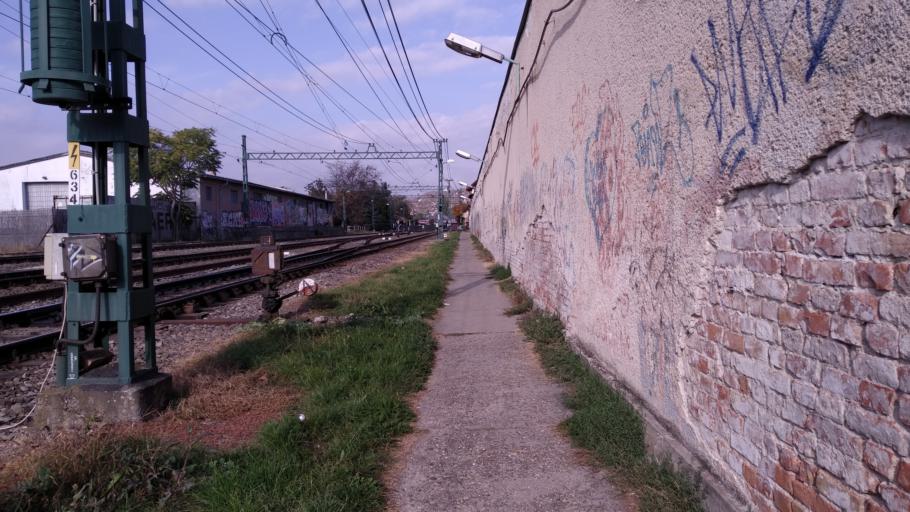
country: HU
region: Pest
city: Pomaz
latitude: 47.6415
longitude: 19.0352
